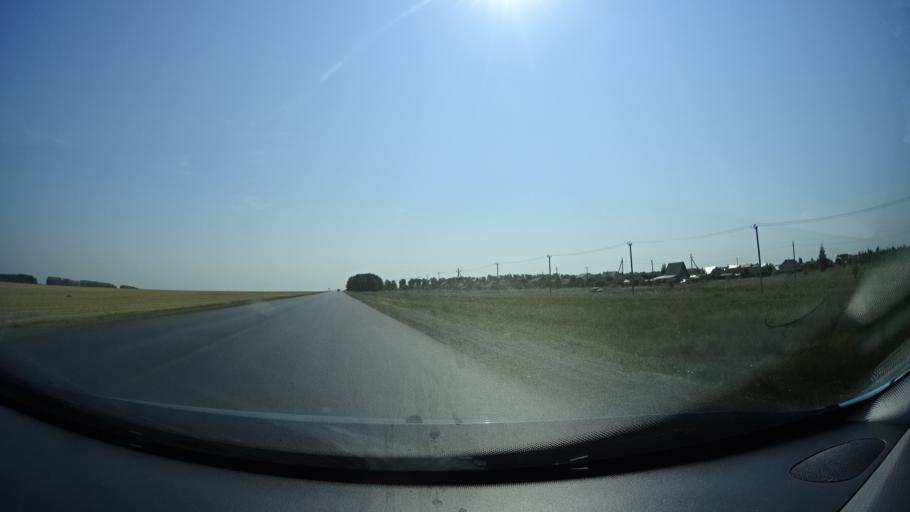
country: RU
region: Bashkortostan
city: Kabakovo
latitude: 54.4779
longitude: 55.9307
